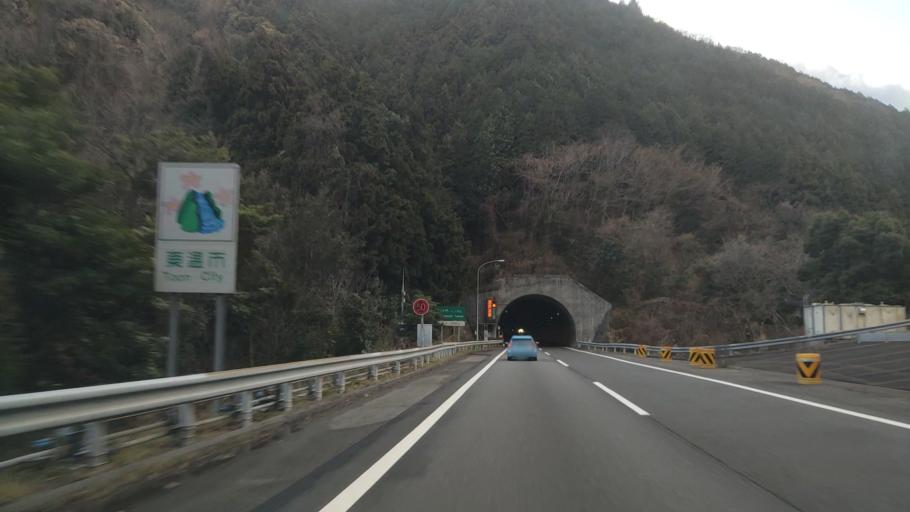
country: JP
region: Ehime
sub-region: Shikoku-chuo Shi
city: Matsuyama
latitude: 33.8267
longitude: 132.9757
